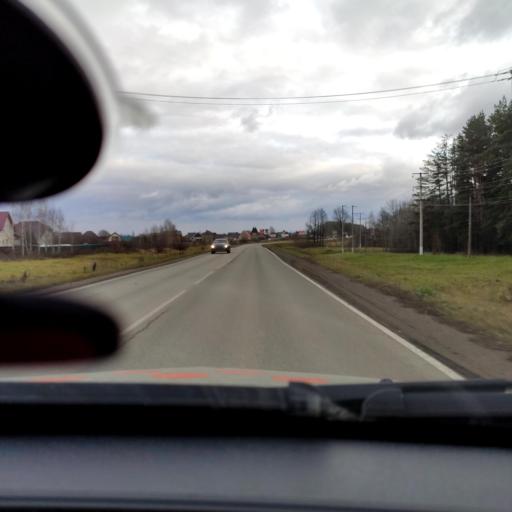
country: RU
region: Bashkortostan
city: Kabakovo
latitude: 54.6132
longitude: 56.1605
